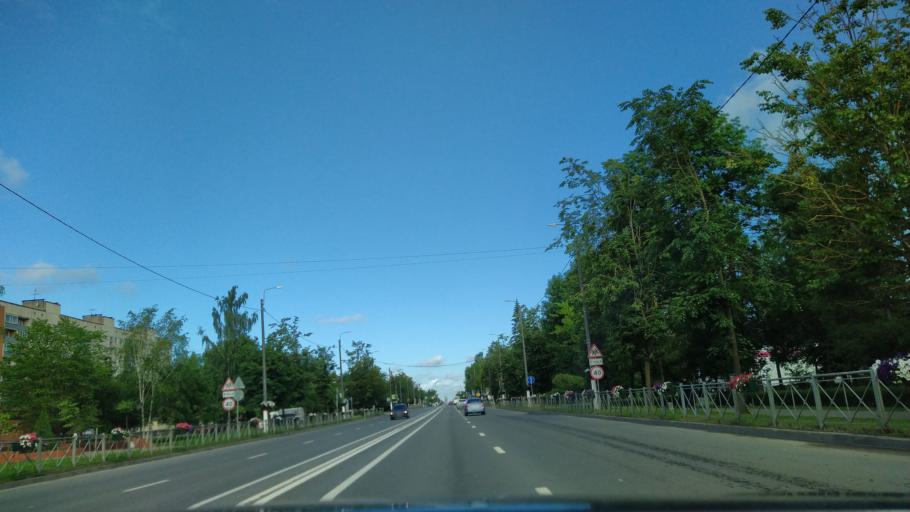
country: RU
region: Leningrad
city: Tosno
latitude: 59.5425
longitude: 30.8742
